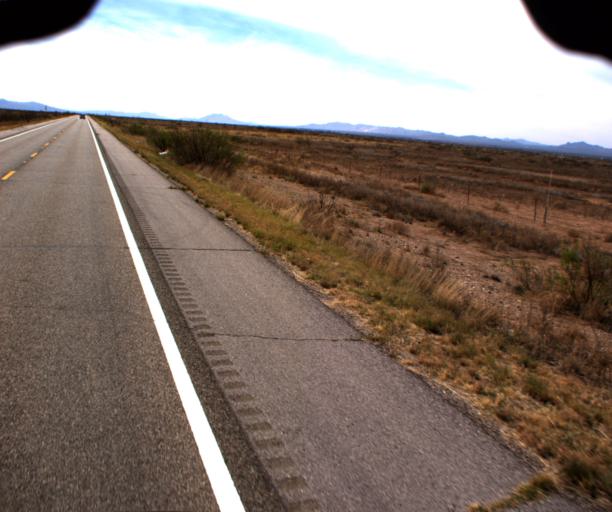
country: US
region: Arizona
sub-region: Cochise County
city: Pirtleville
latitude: 31.5147
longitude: -109.6429
